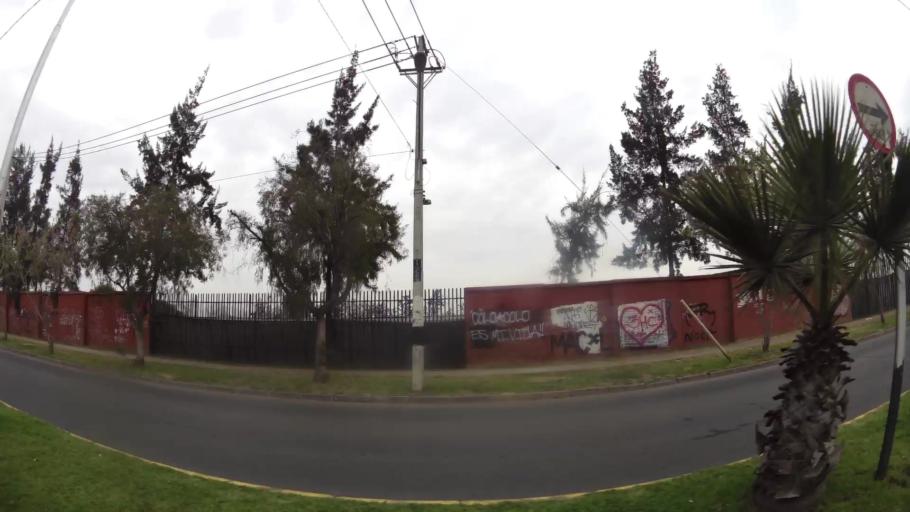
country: CL
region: Santiago Metropolitan
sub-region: Provincia de Santiago
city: Villa Presidente Frei, Nunoa, Santiago, Chile
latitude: -33.5040
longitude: -70.6034
